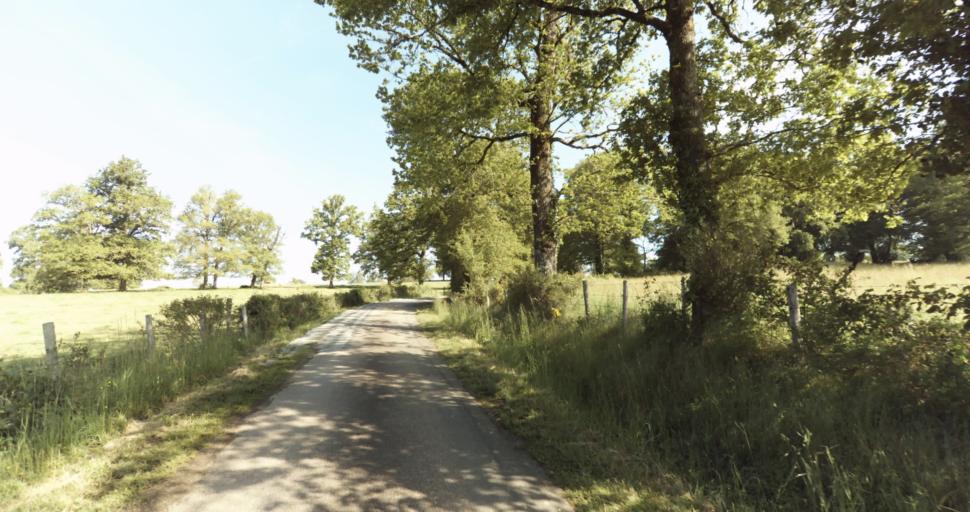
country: FR
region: Limousin
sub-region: Departement de la Haute-Vienne
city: Solignac
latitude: 45.7003
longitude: 1.2552
